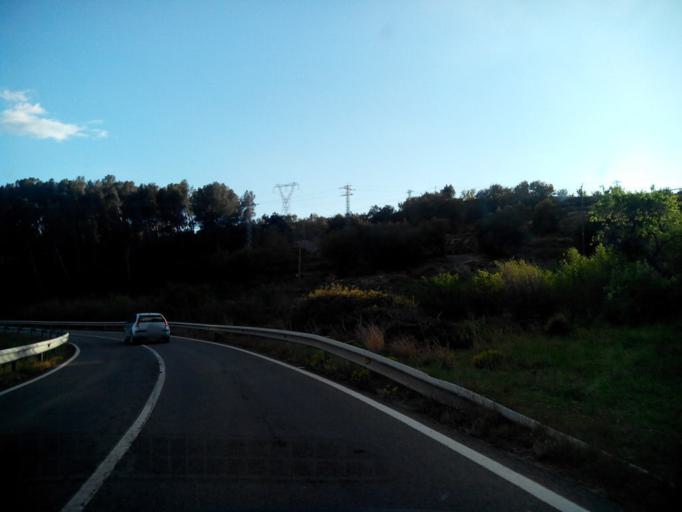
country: ES
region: Catalonia
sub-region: Provincia de Tarragona
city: les Borges del Camp
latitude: 41.1897
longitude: 1.0462
